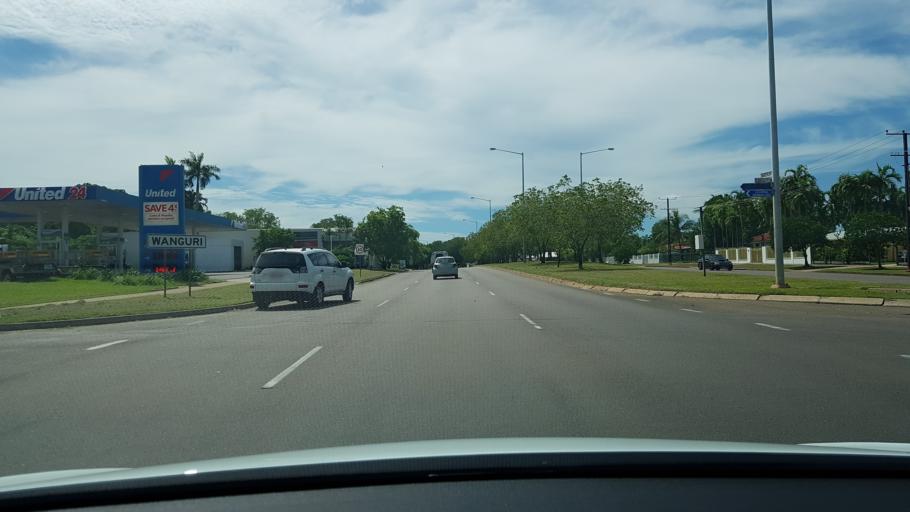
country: AU
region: Northern Territory
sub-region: Darwin
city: Leanyer
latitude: -12.3763
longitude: 130.8846
